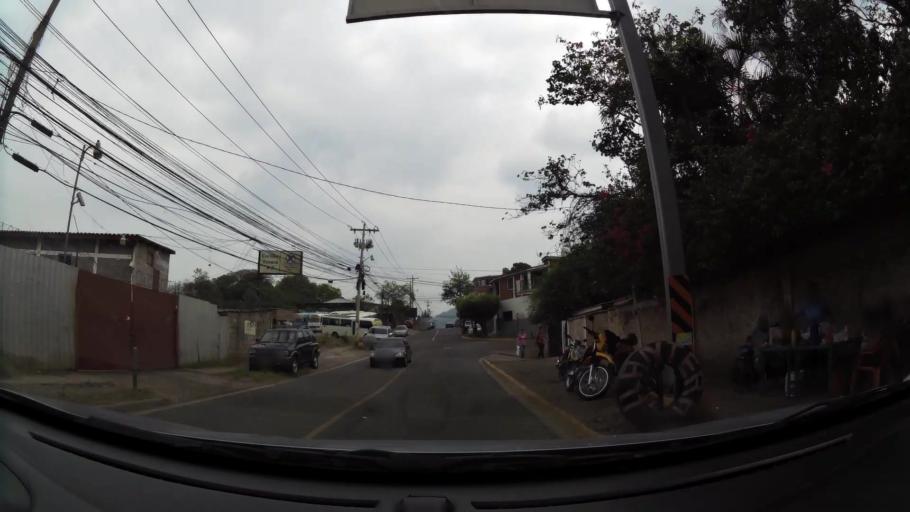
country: HN
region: Francisco Morazan
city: Tegucigalpa
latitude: 14.1013
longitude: -87.1747
